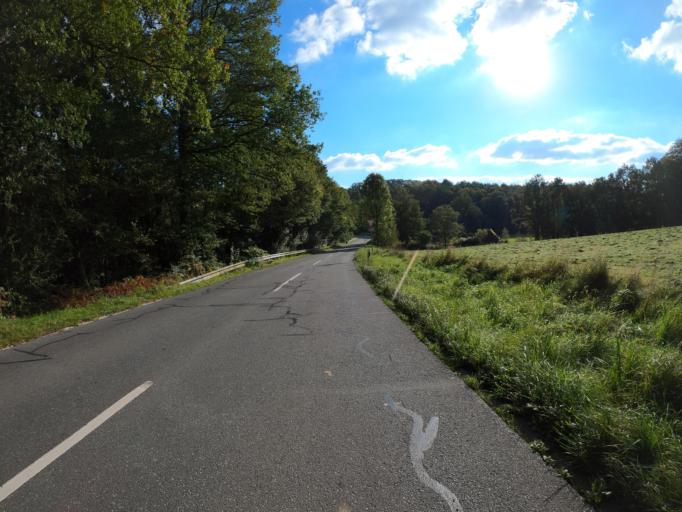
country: DE
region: North Rhine-Westphalia
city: Radevormwald
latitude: 51.2149
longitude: 7.3510
